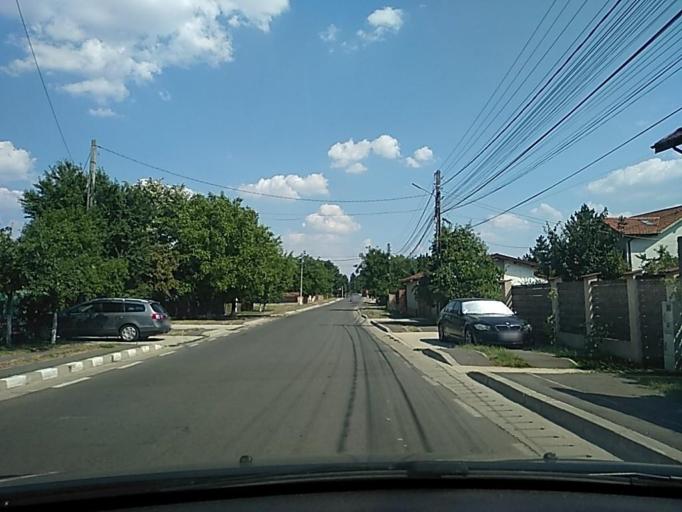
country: RO
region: Ilfov
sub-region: Comuna Domnesti
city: Domnesti
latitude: 44.4058
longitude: 25.9311
